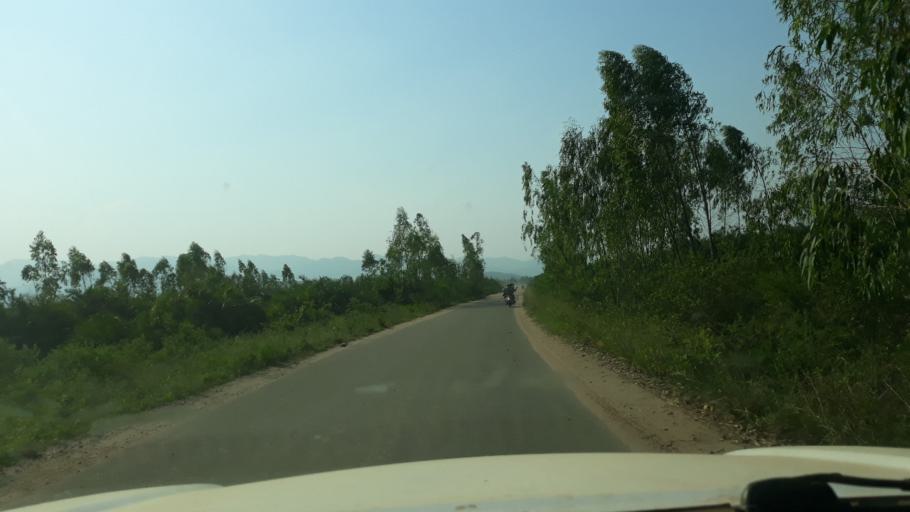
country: BI
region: Cibitoke
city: Cibitoke
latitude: -2.8098
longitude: 29.0018
